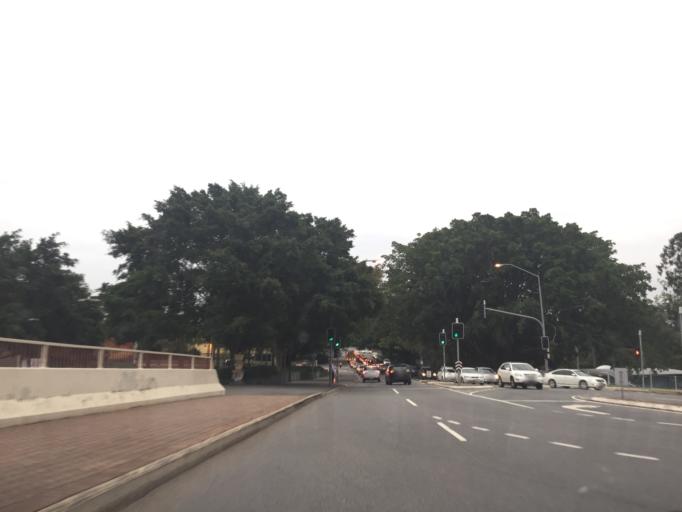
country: AU
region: Queensland
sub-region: Brisbane
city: Milton
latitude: -27.4635
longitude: 153.0112
